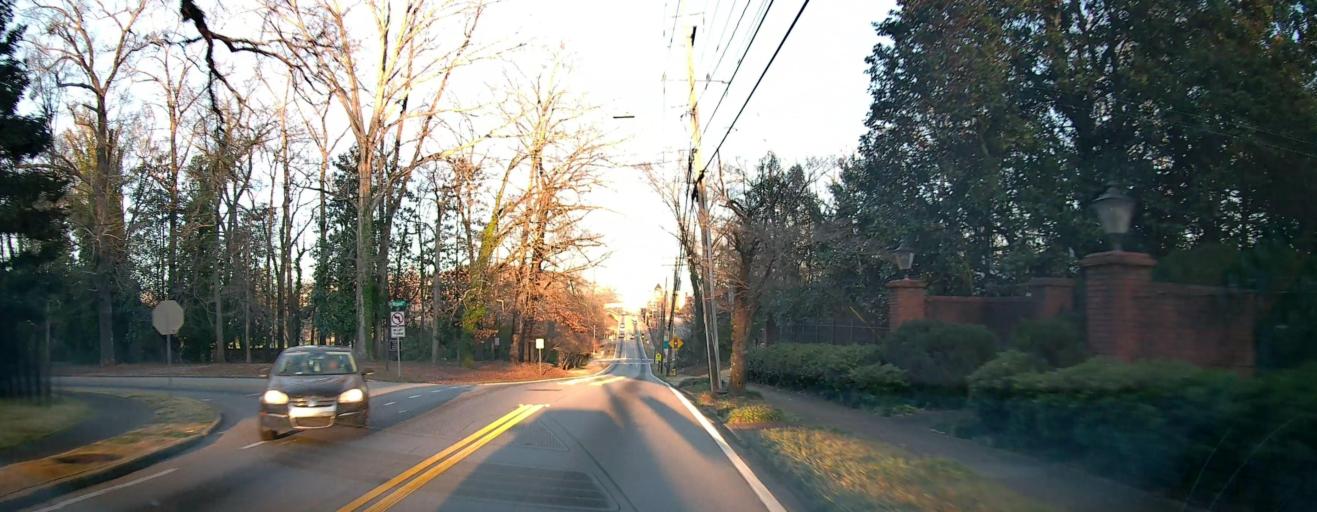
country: US
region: Georgia
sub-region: Troup County
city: La Grange
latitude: 33.0371
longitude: -85.0469
